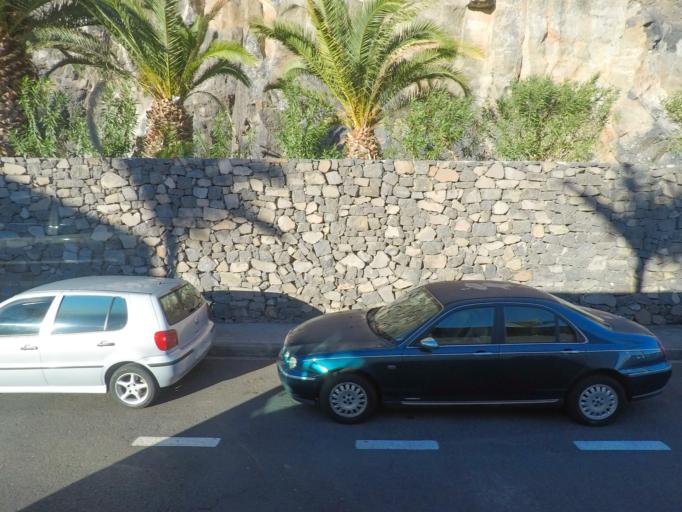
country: ES
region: Canary Islands
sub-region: Provincia de Santa Cruz de Tenerife
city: San Sebastian de la Gomera
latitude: 28.0899
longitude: -17.1086
